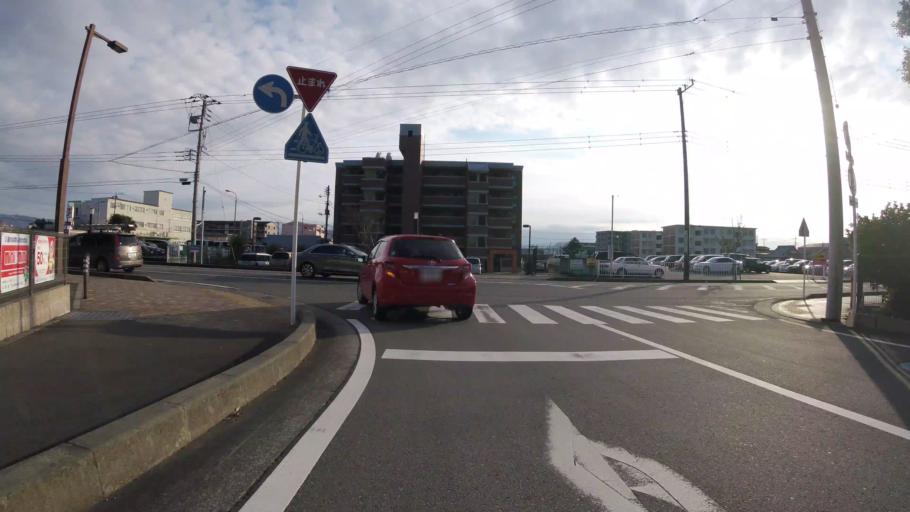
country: JP
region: Shizuoka
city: Mishima
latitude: 35.1290
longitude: 138.9062
